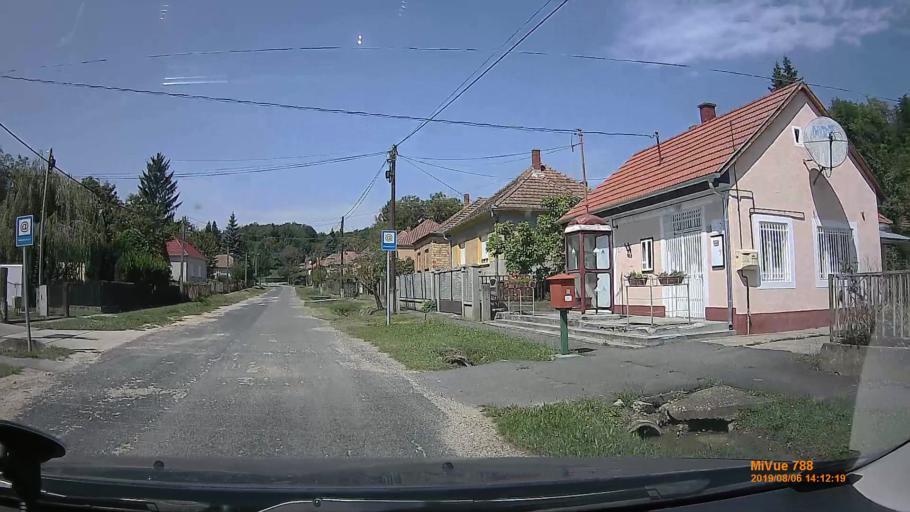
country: HU
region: Zala
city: Zalakomar
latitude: 46.5611
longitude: 17.0780
